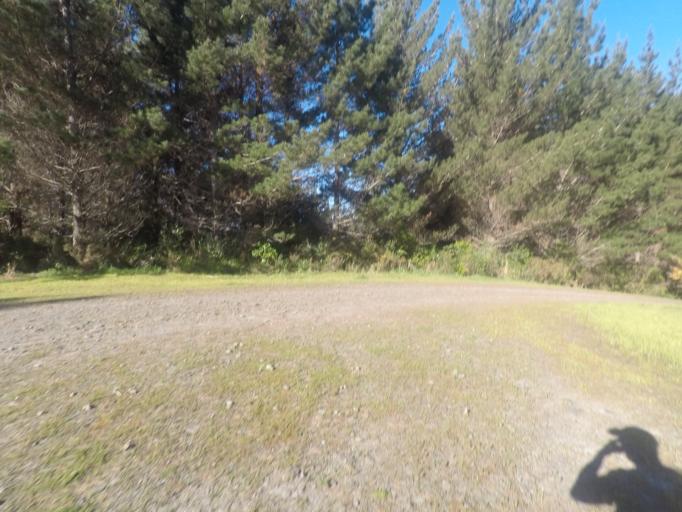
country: NZ
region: Auckland
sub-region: Auckland
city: Muriwai Beach
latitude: -36.7449
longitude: 174.5566
